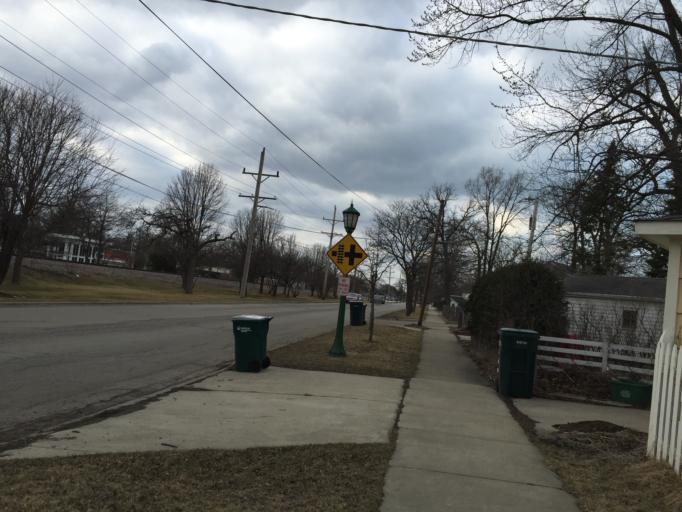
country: US
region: Illinois
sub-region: Cook County
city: Wilmette
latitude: 42.0708
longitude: -87.7034
